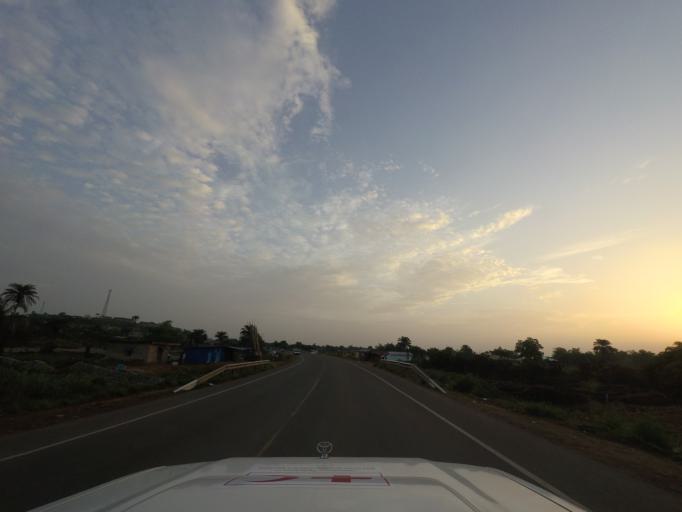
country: LR
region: Montserrado
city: Bensonville City
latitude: 6.3303
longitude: -10.6589
